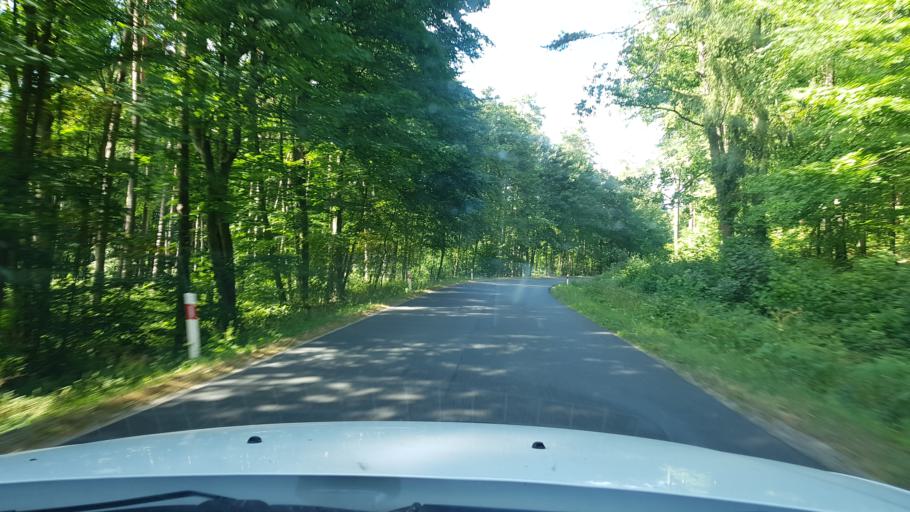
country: PL
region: West Pomeranian Voivodeship
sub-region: Powiat drawski
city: Zlocieniec
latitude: 53.5626
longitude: 16.0100
